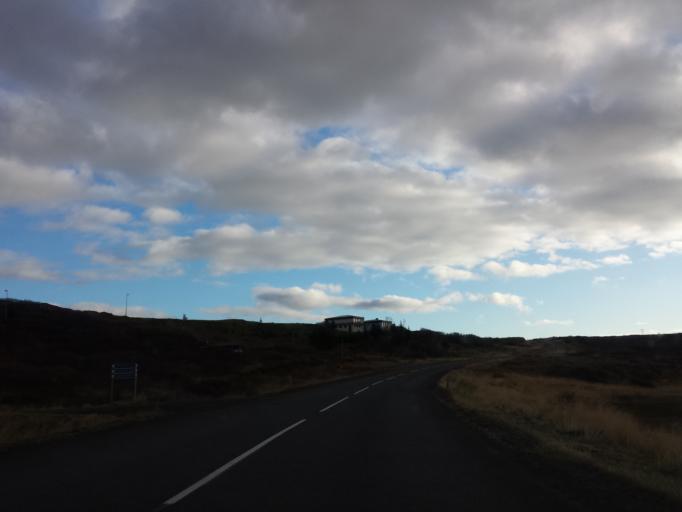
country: IS
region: West
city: Borgarnes
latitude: 64.5898
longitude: -21.9847
